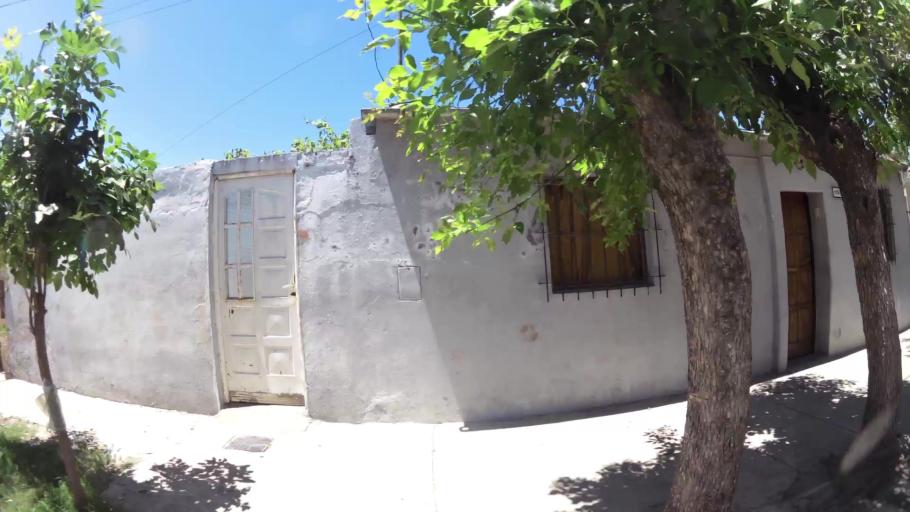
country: AR
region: Santa Fe
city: Santo Tome
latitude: -31.6546
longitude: -60.7305
